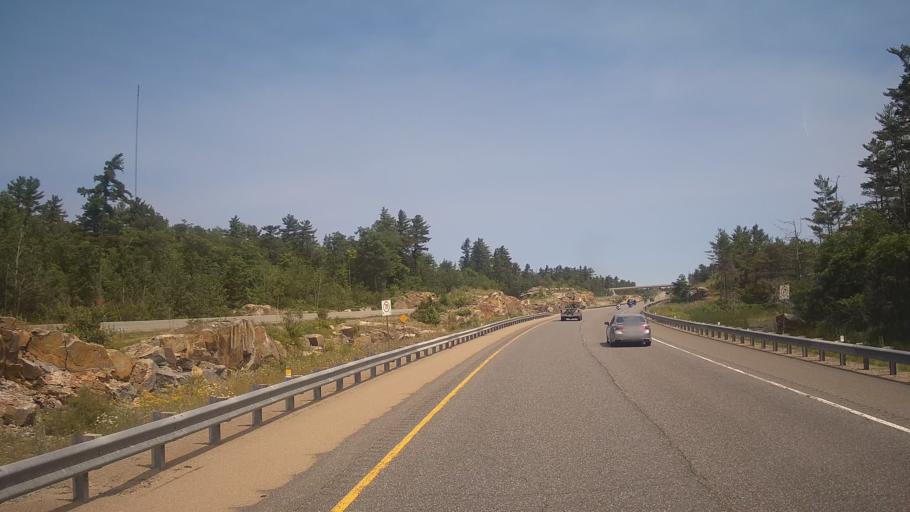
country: CA
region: Ontario
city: Midland
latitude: 44.9600
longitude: -79.7788
